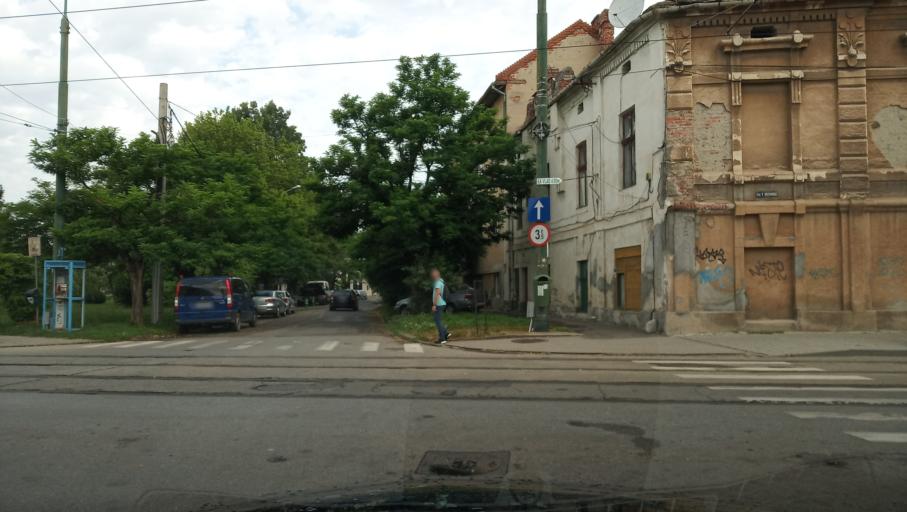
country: RO
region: Timis
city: Timisoara
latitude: 45.7418
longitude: 21.2326
